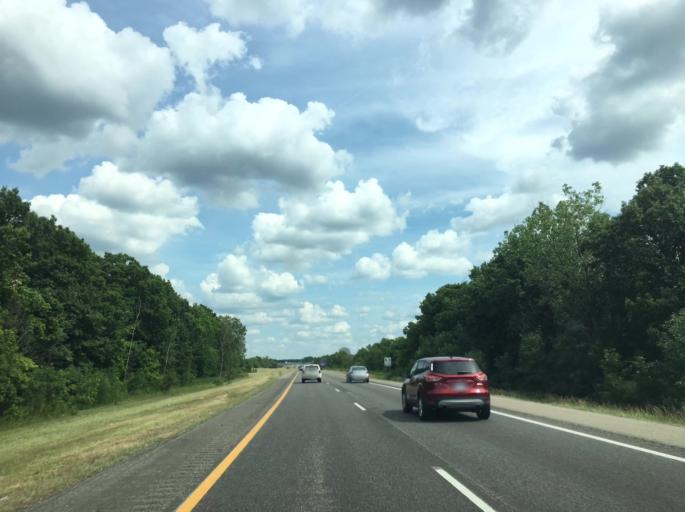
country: US
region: Michigan
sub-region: Genesee County
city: Grand Blanc
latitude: 42.9215
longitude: -83.6836
